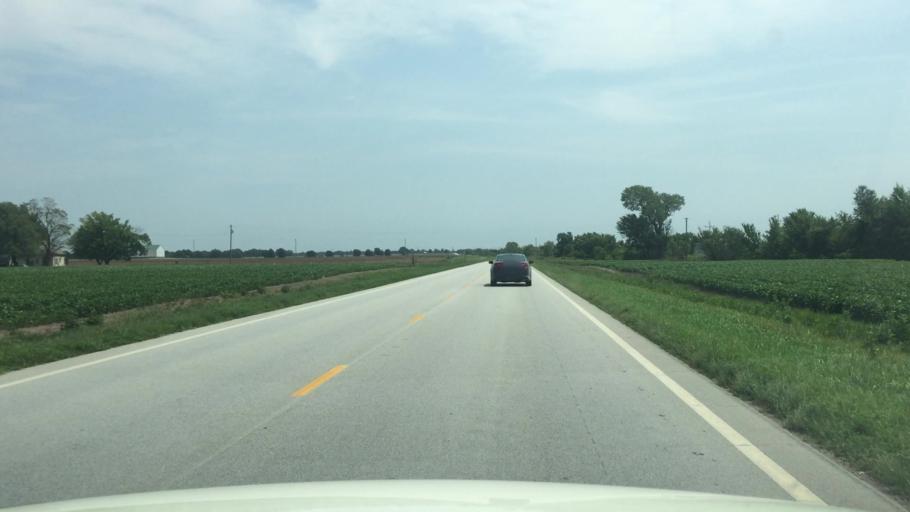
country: US
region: Kansas
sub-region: Cherokee County
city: Columbus
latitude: 37.1797
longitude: -94.9433
